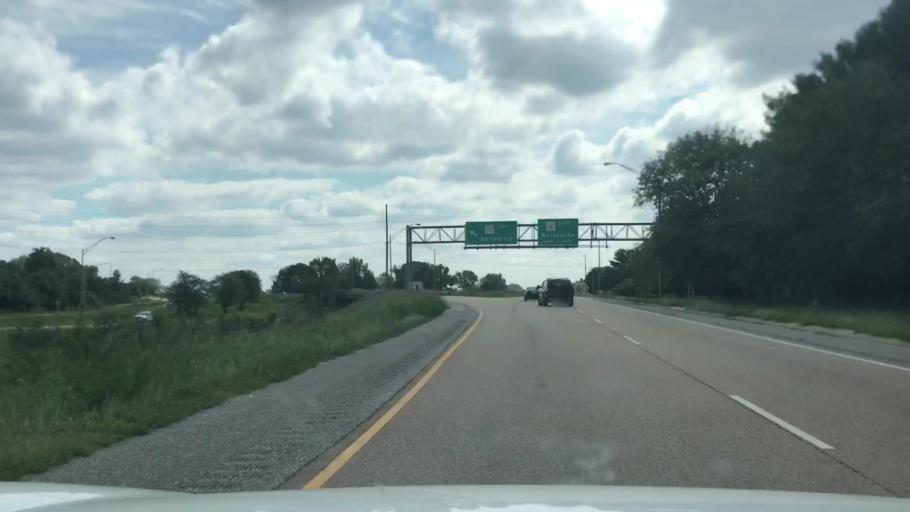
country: US
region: Illinois
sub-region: Saint Clair County
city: Alorton
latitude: 38.5493
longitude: -90.0691
